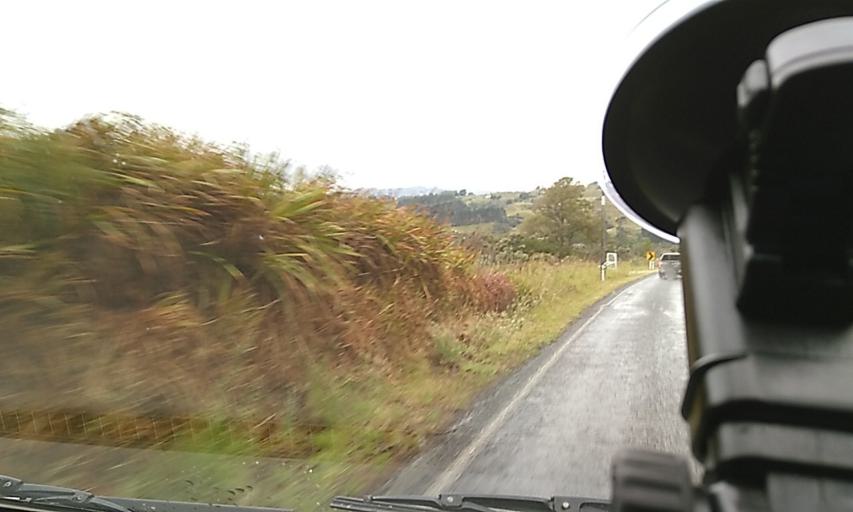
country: NZ
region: Auckland
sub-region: Auckland
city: Pukekohe East
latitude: -37.2988
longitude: 174.9377
